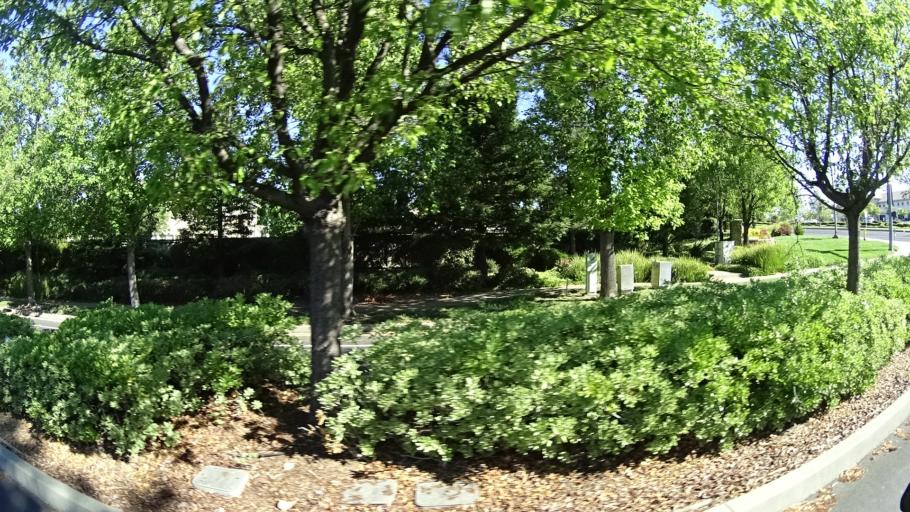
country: US
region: California
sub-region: Placer County
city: Rocklin
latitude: 38.7898
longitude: -121.2699
